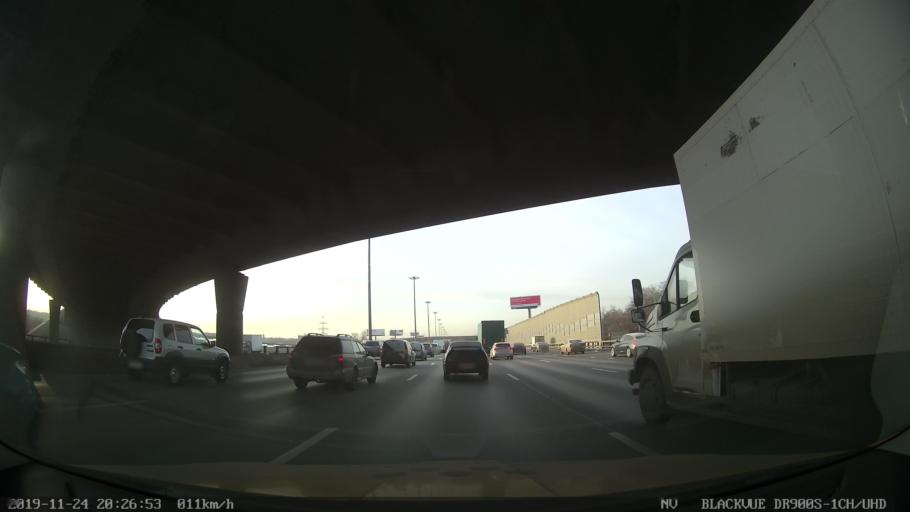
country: RU
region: Moskovskaya
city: Druzhba
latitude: 55.8998
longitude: 37.7542
